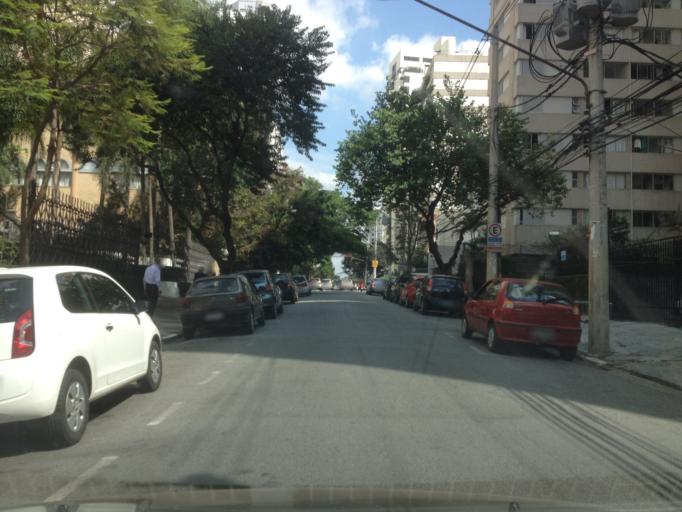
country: BR
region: Sao Paulo
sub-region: Sao Paulo
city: Sao Paulo
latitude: -23.5704
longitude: -46.6488
